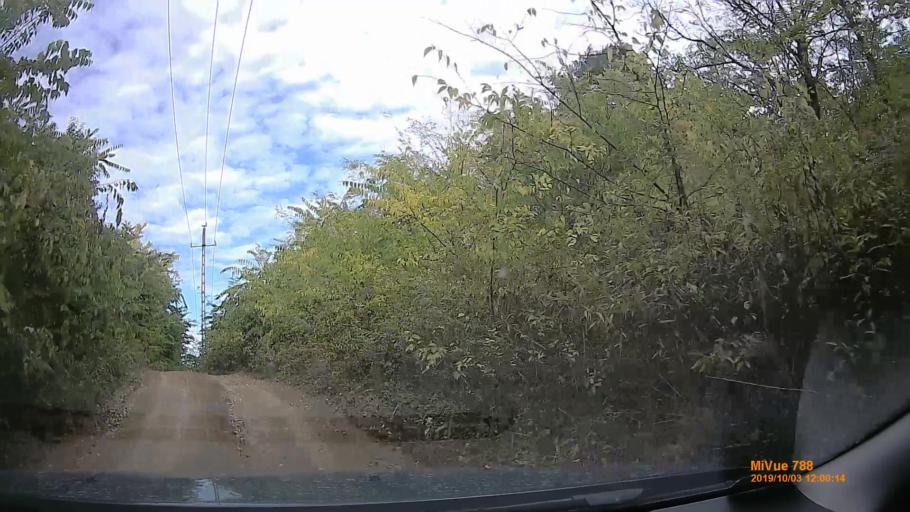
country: HU
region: Pest
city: God
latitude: 47.6731
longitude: 19.1719
